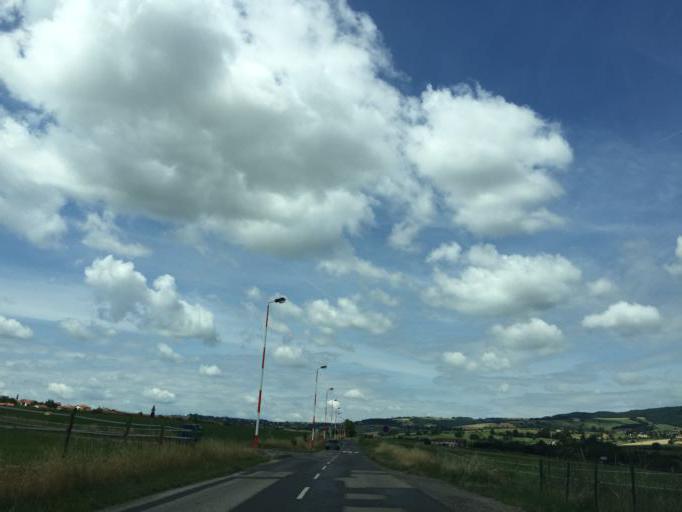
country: FR
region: Rhone-Alpes
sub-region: Departement de la Loire
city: La Grand-Croix
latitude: 45.4925
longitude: 4.5406
